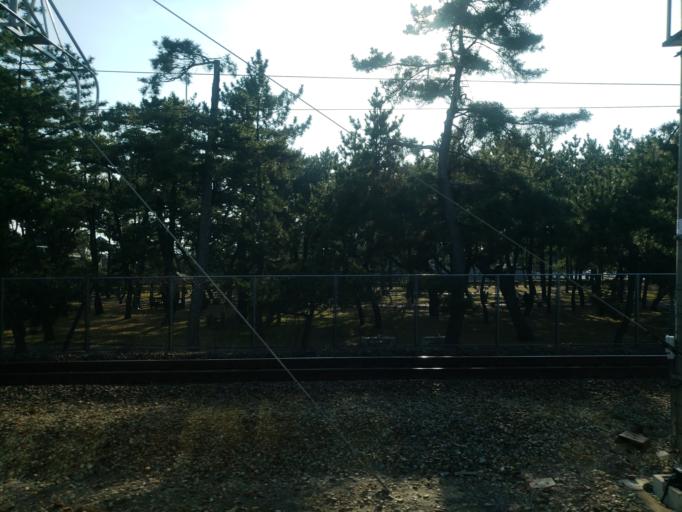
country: JP
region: Hyogo
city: Akashi
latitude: 34.6316
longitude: 135.0364
